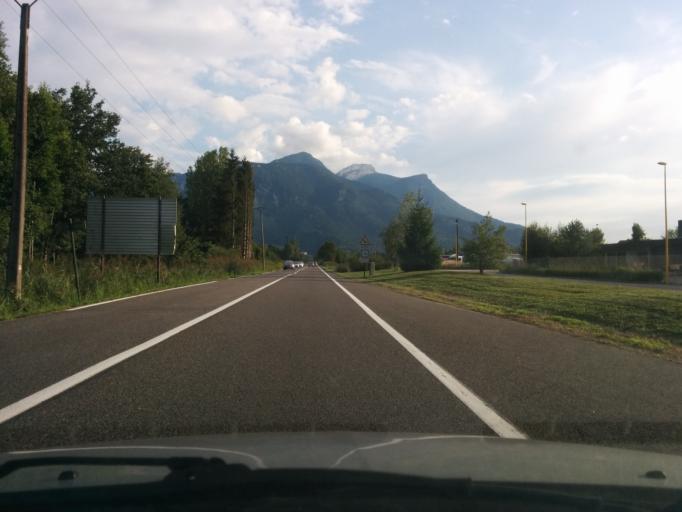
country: FR
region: Rhone-Alpes
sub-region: Departement de l'Isere
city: Entre-deux-Guiers
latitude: 45.4122
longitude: 5.7489
